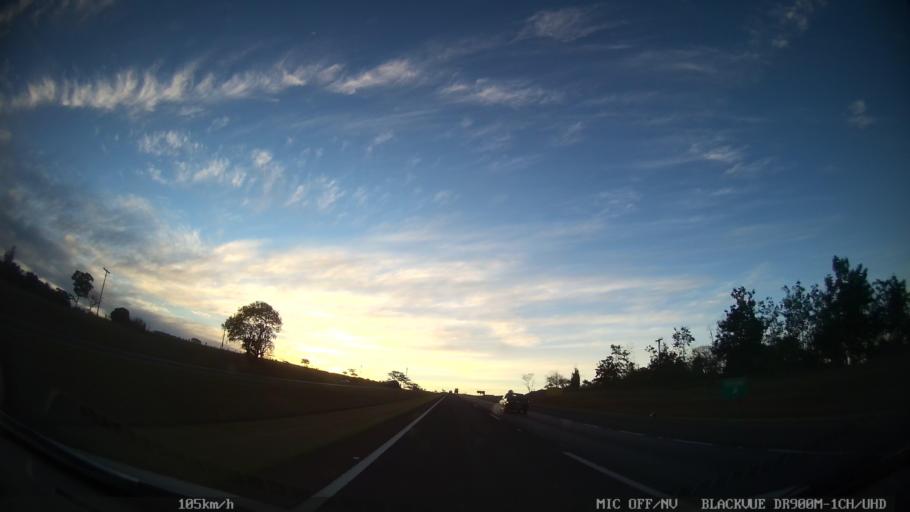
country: BR
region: Sao Paulo
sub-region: Catanduva
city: Catanduva
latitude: -21.1798
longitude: -48.9617
